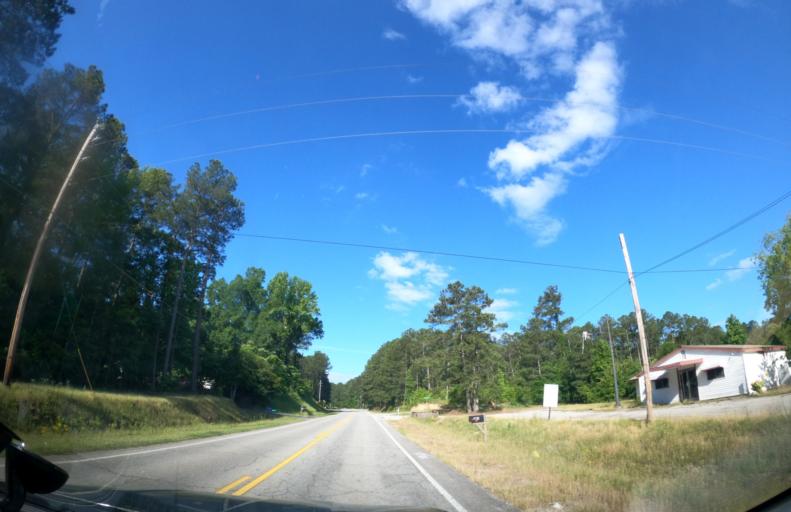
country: US
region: Georgia
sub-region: Columbia County
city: Harlem
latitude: 33.4410
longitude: -82.2712
